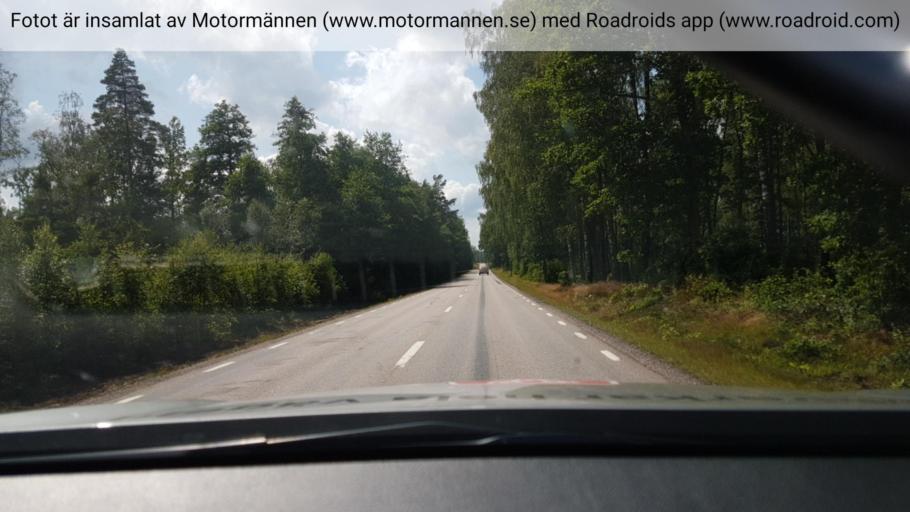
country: SE
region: Vaestra Goetaland
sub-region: Svenljunga Kommun
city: Svenljunga
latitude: 57.4962
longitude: 13.0823
